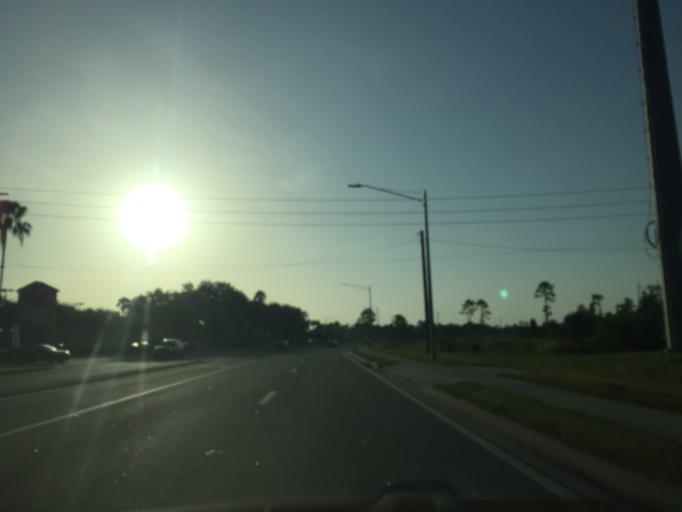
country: US
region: Florida
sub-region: Orange County
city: Alafaya
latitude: 28.5247
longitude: -81.1951
